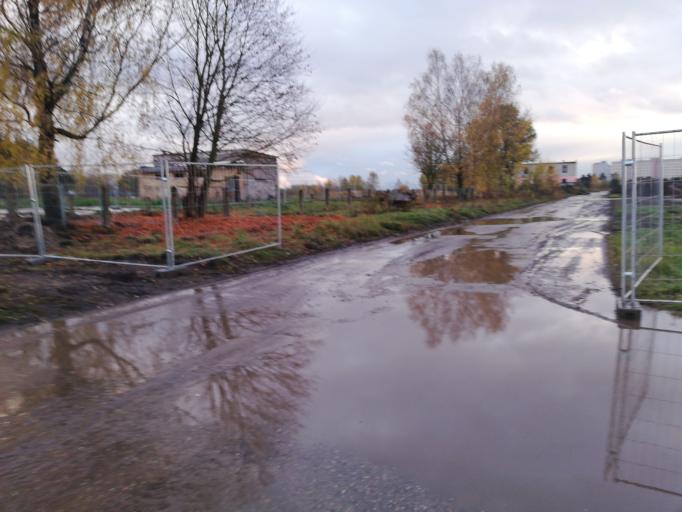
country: LV
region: Stopini
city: Ulbroka
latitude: 56.9526
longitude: 24.2368
